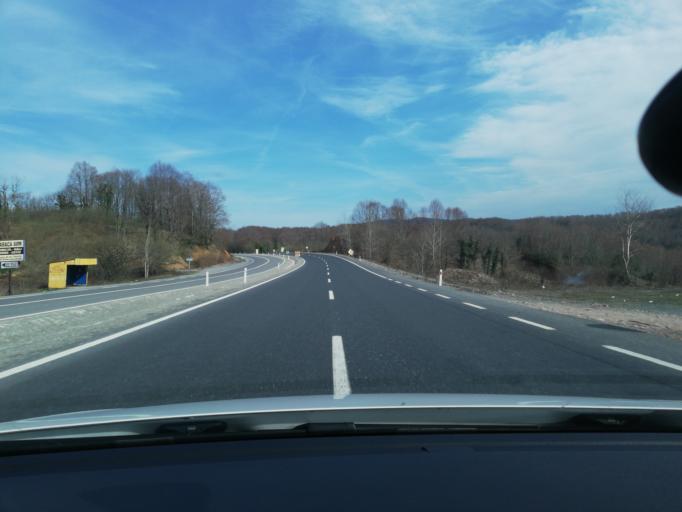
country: TR
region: Zonguldak
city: Kozlu
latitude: 41.3325
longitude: 31.6179
